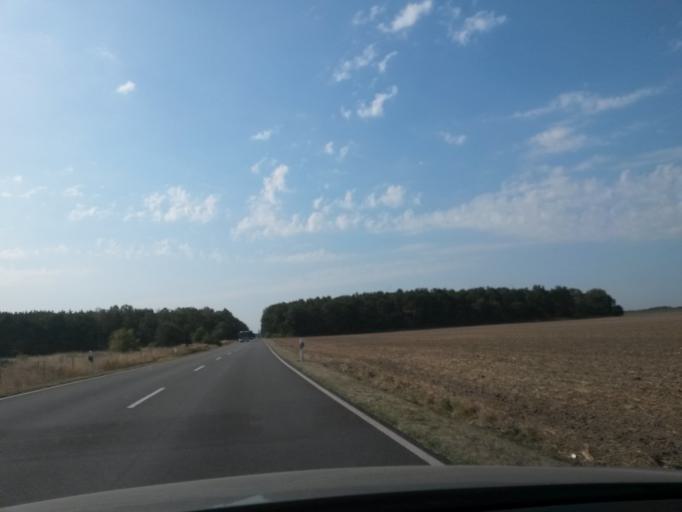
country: DE
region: Saxony-Anhalt
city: Jerichow
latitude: 52.5344
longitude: 12.0160
